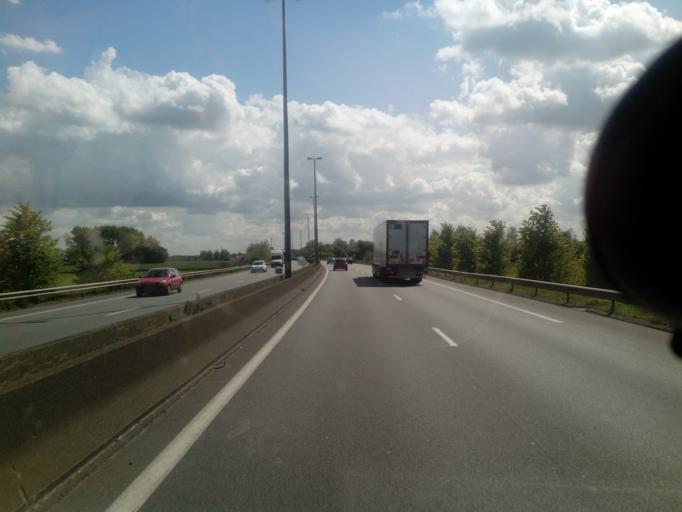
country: FR
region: Nord-Pas-de-Calais
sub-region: Departement du Nord
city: Loon-Plage
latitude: 50.9816
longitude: 2.2264
